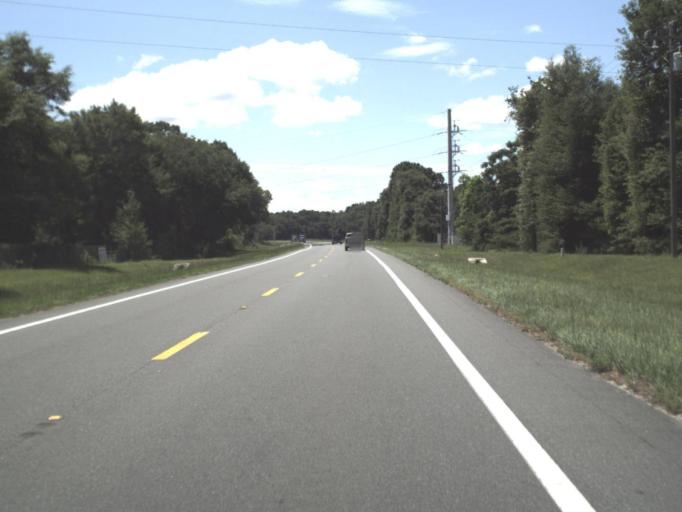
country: US
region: Florida
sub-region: Lafayette County
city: Mayo
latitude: 30.1201
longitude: -83.2637
